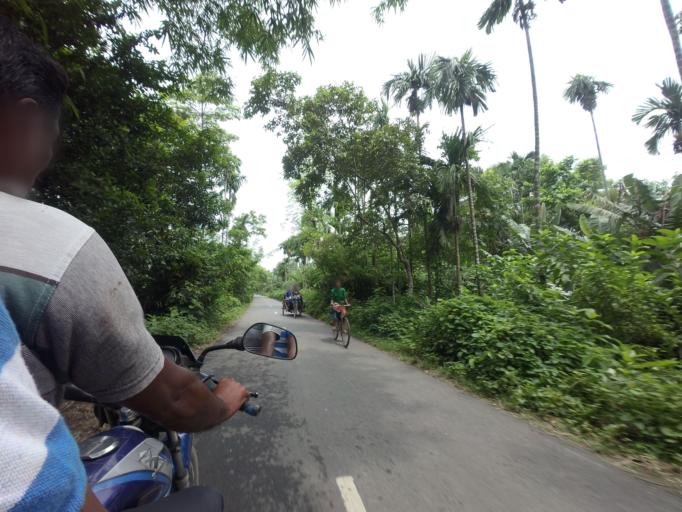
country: BD
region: Khulna
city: Kalia
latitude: 23.0871
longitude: 89.6633
